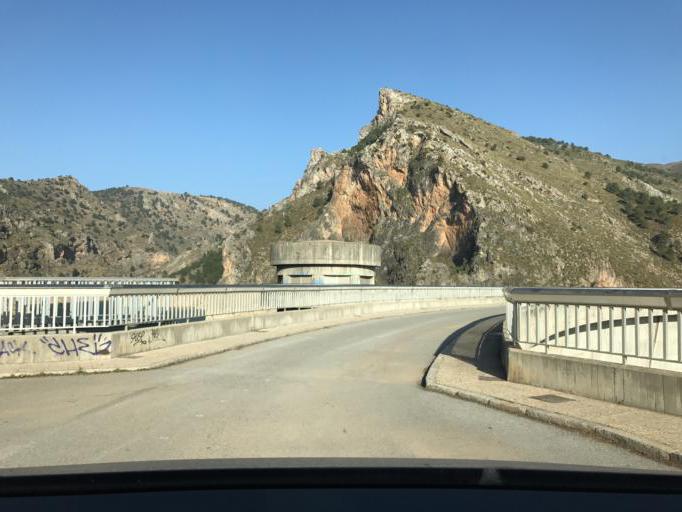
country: ES
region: Andalusia
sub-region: Provincia de Granada
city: Quentar
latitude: 37.2035
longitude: -3.4389
